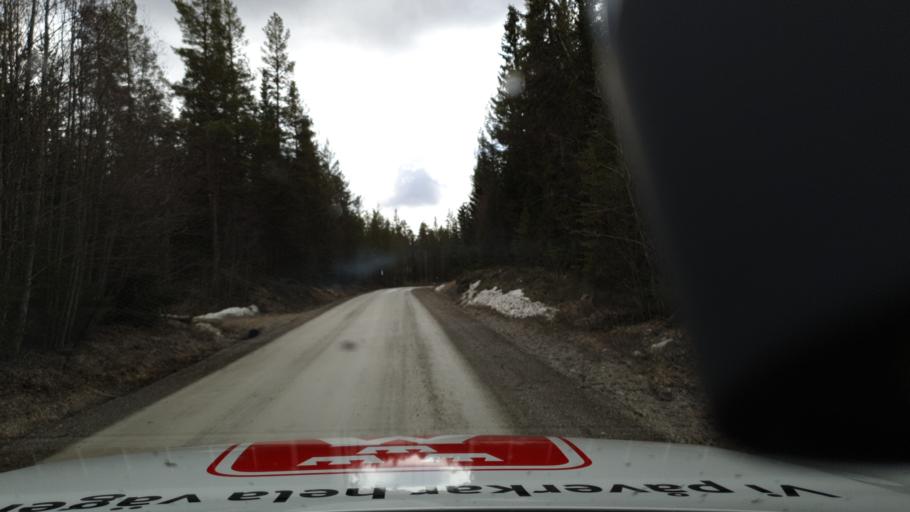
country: SE
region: Jaemtland
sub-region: Bergs Kommun
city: Hoverberg
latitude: 62.7711
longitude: 13.8287
